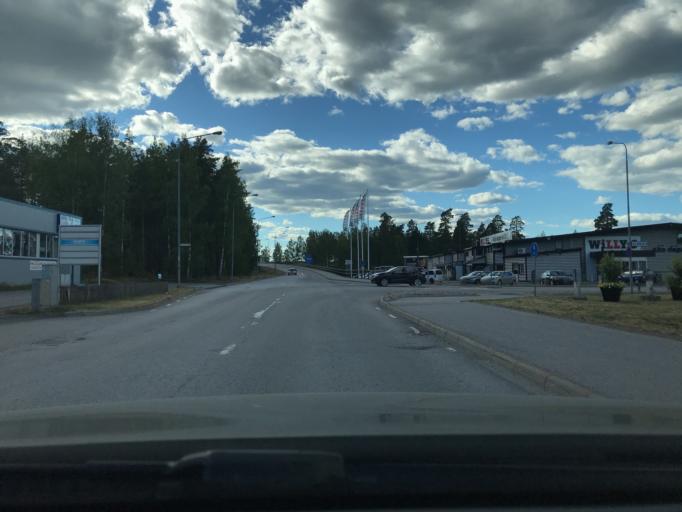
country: SE
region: Kalmar
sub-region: Hultsfreds Kommun
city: Hultsfred
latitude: 57.4987
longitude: 15.8271
